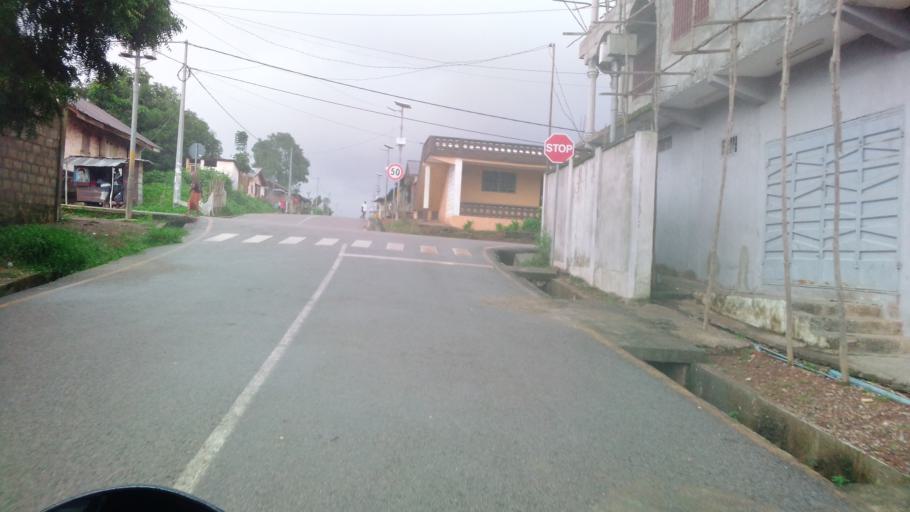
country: SL
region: Northern Province
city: Lunsar
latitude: 8.6831
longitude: -12.5335
